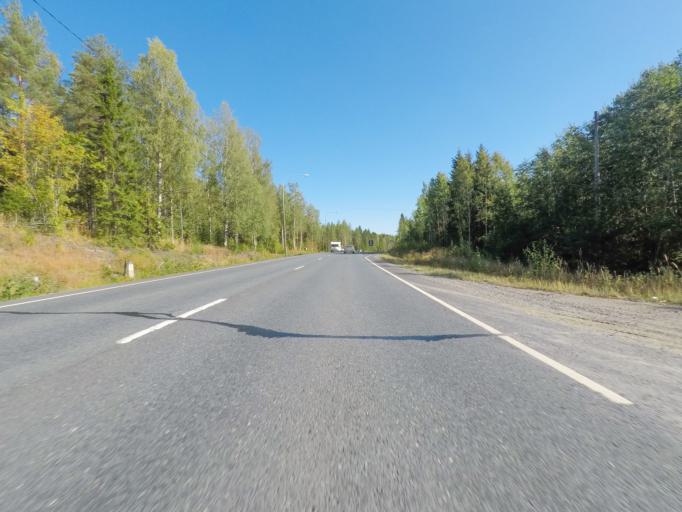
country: FI
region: Northern Savo
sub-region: Varkaus
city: Leppaevirta
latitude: 62.5005
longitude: 27.7396
